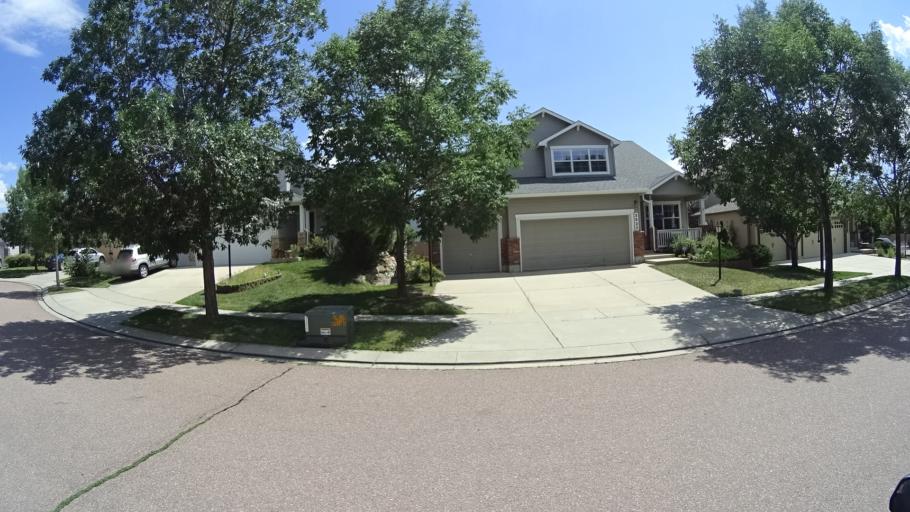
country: US
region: Colorado
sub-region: El Paso County
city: Black Forest
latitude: 38.9677
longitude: -104.7612
